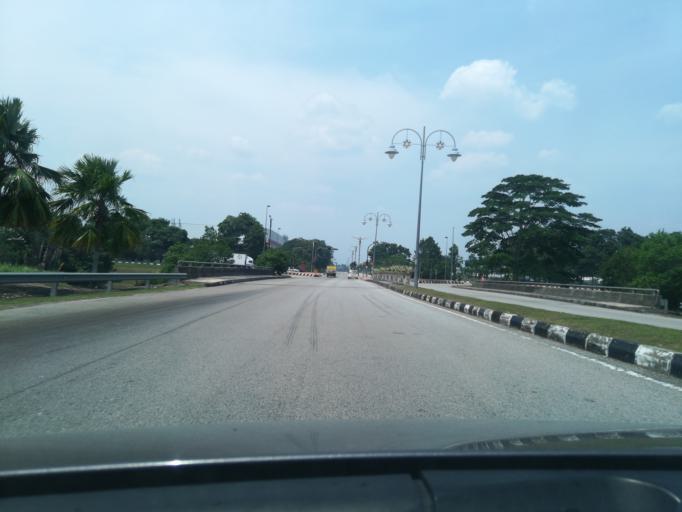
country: MY
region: Kedah
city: Kulim
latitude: 5.4252
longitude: 100.5811
